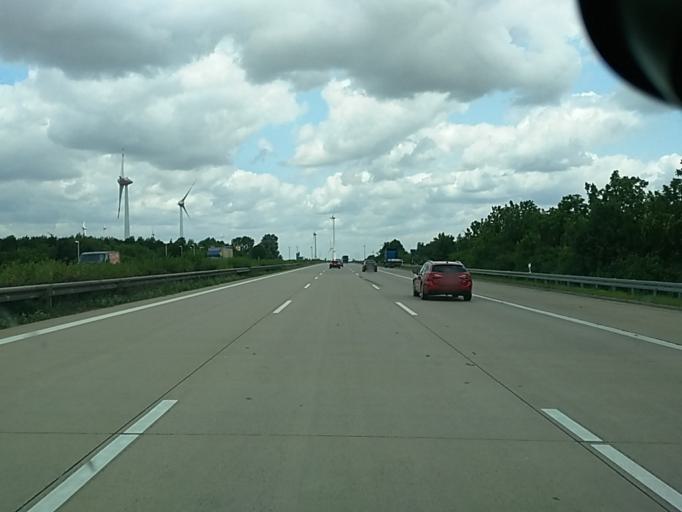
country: DE
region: Saxony-Anhalt
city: Stossen
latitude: 51.1069
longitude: 11.9559
